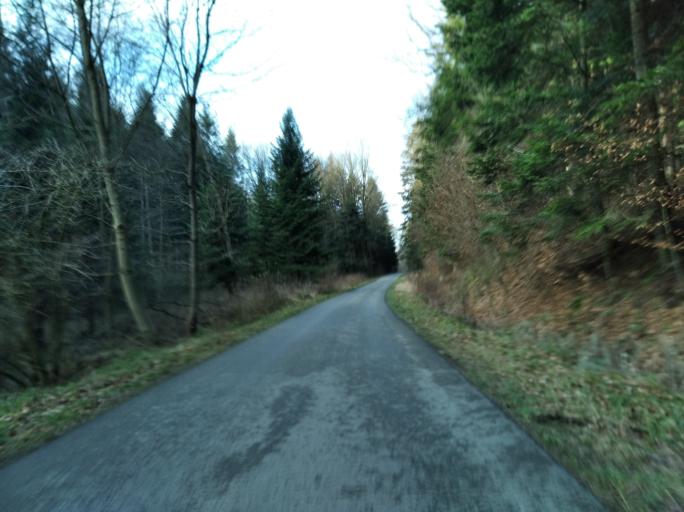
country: PL
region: Subcarpathian Voivodeship
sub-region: Powiat strzyzowski
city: Konieczkowa
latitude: 49.8263
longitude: 21.9428
